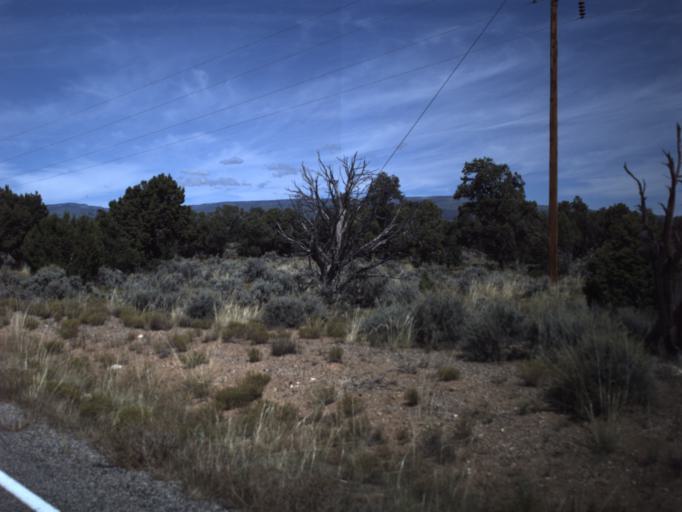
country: US
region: Utah
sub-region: Wayne County
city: Loa
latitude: 37.8496
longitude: -111.4289
